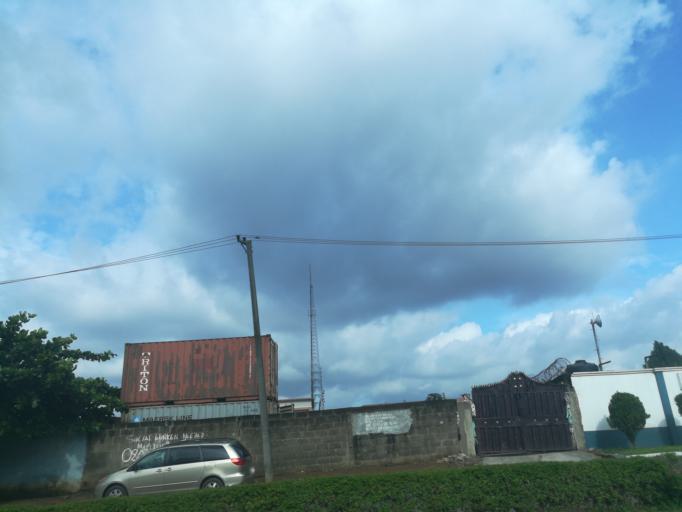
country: NG
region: Lagos
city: Ikeja
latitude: 6.6195
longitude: 3.3581
